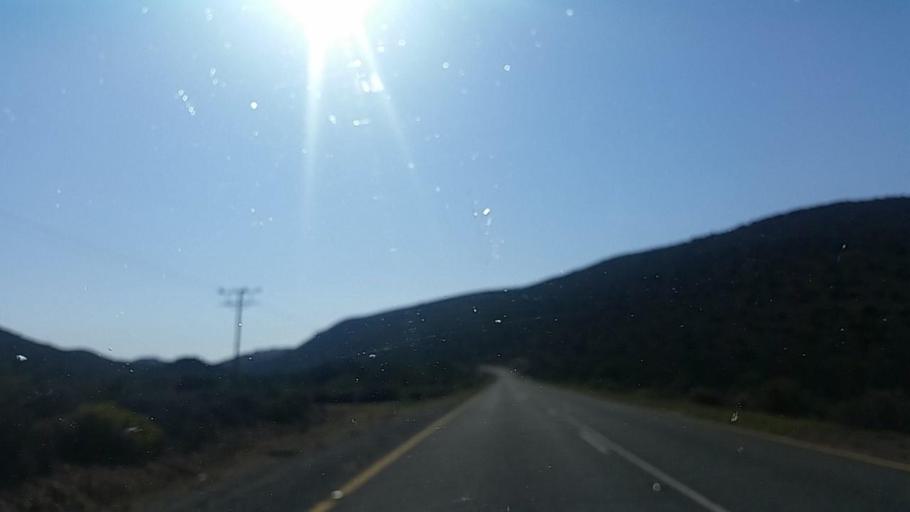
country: ZA
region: Eastern Cape
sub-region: Cacadu District Municipality
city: Willowmore
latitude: -33.3881
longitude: 23.3839
